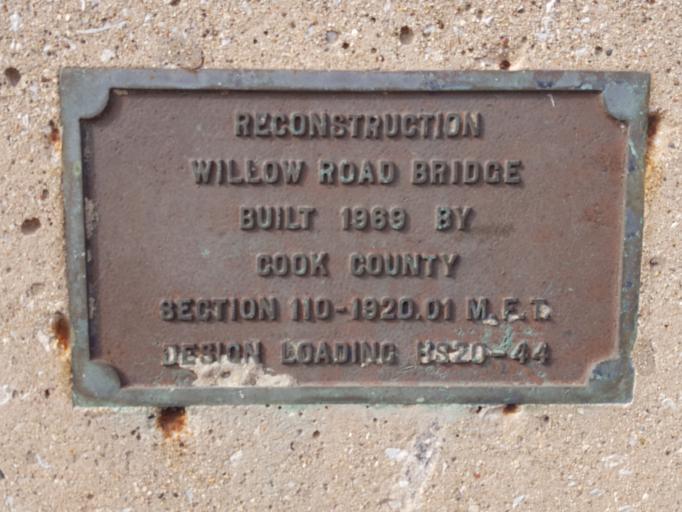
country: US
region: Illinois
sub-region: Cook County
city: Northbrook
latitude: 42.1056
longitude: -87.8105
